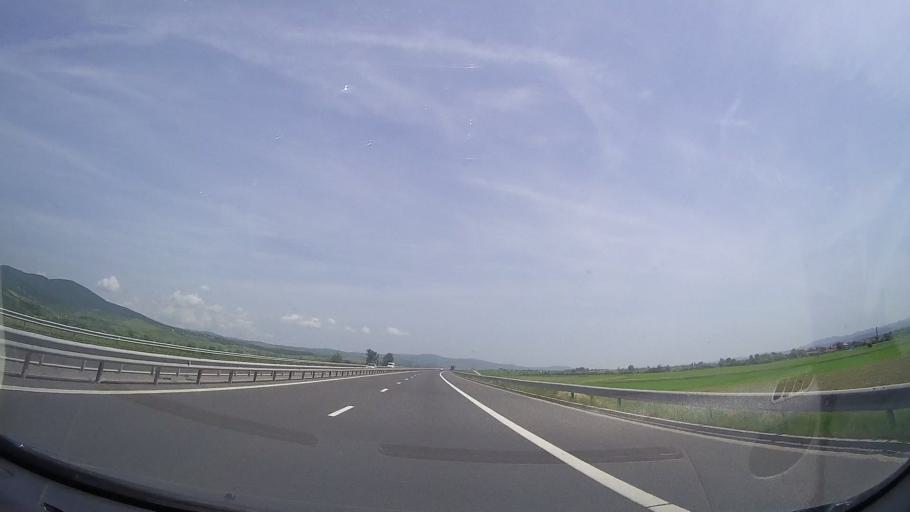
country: RO
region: Hunedoara
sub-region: Comuna Turdas
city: Pricaz
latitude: 45.8657
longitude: 23.1550
